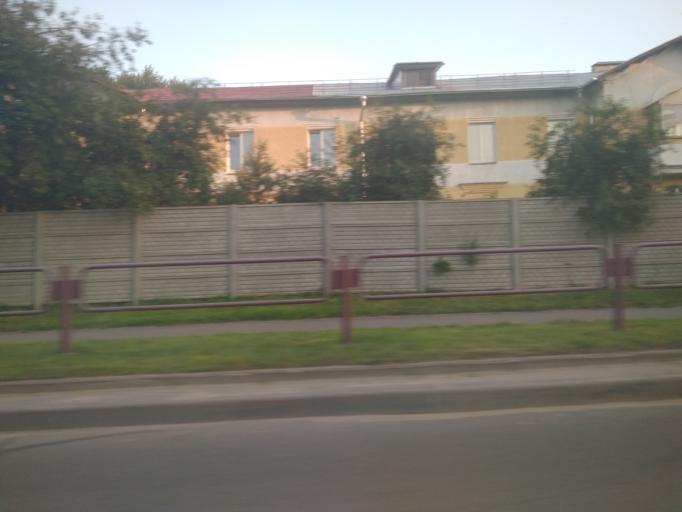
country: BY
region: Minsk
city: Zhdanovichy
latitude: 53.9300
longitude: 27.4742
